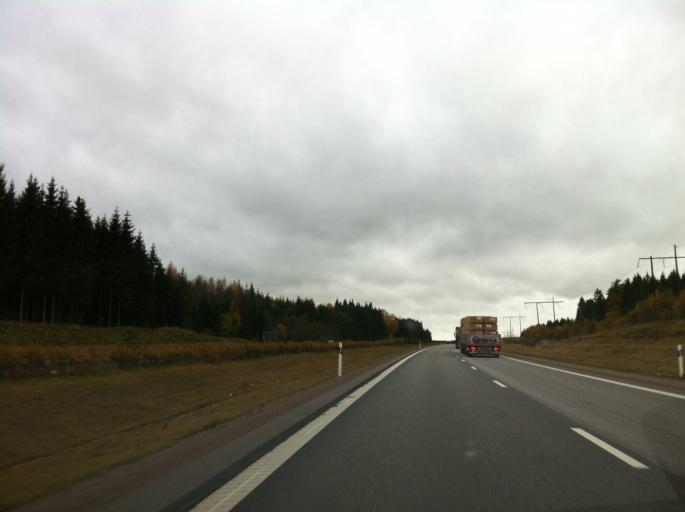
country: SE
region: OEstergoetland
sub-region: Vadstena Kommun
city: Herrestad
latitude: 58.2942
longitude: 14.9177
